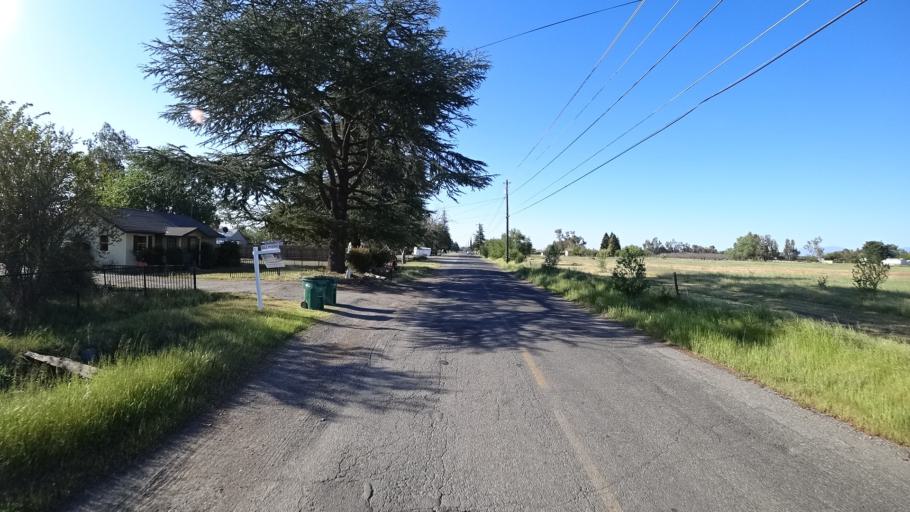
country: US
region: California
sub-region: Glenn County
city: Orland
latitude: 39.7340
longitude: -122.1875
